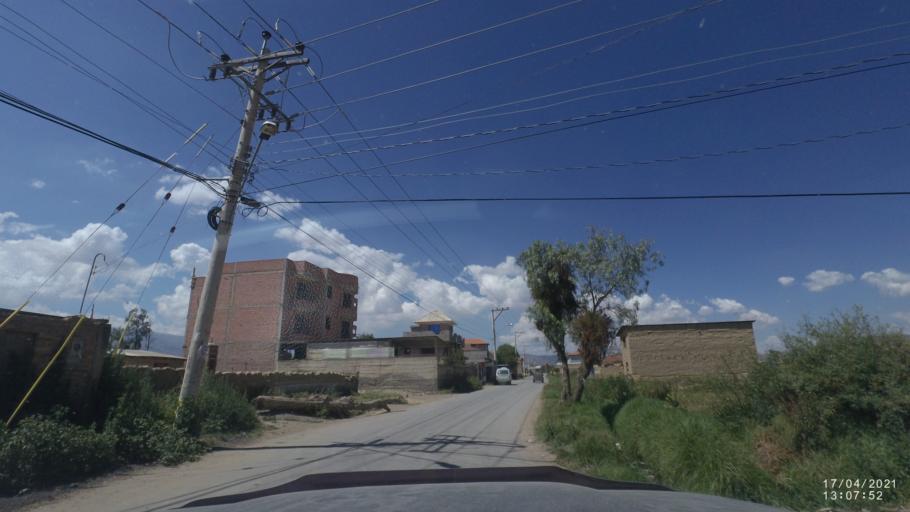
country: BO
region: Cochabamba
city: Cochabamba
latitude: -17.4142
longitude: -66.2236
